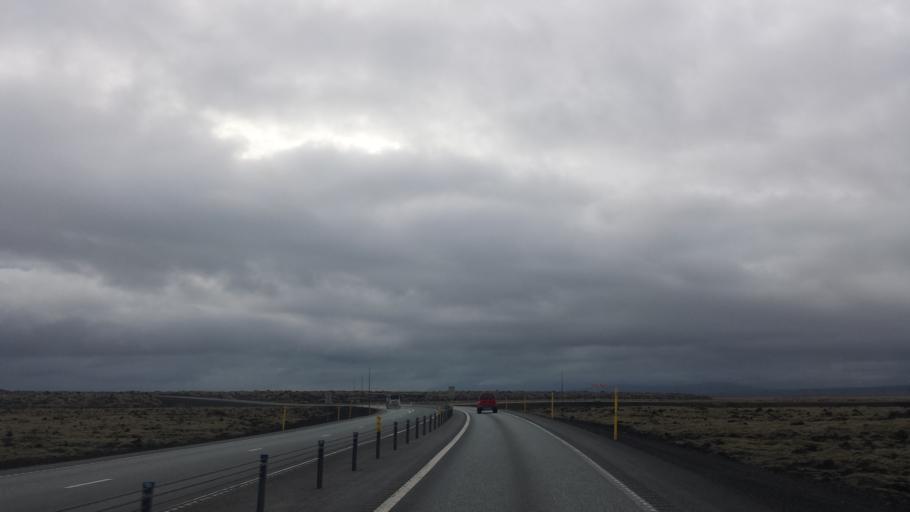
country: IS
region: South
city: THorlakshoefn
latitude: 64.0274
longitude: -21.4201
